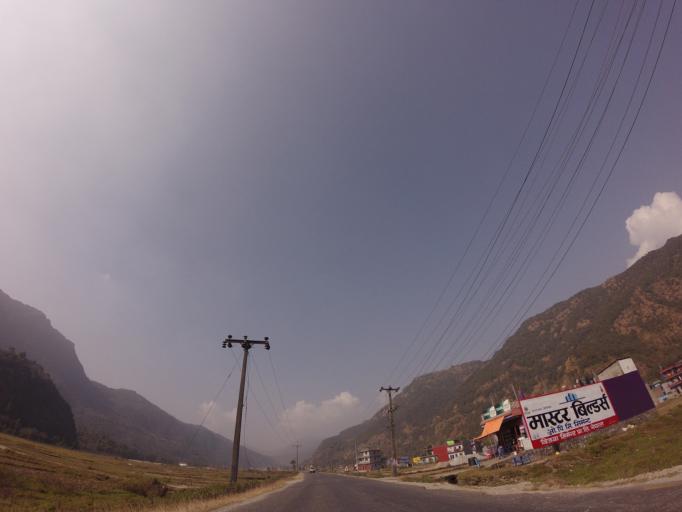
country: NP
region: Western Region
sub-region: Gandaki Zone
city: Pokhara
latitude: 28.2833
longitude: 83.9219
